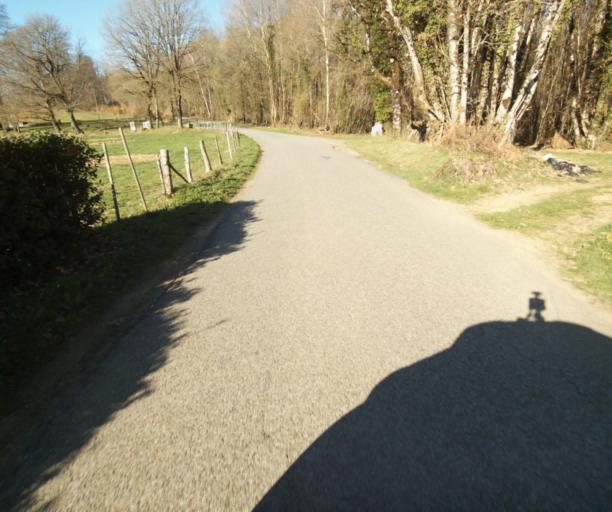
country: FR
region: Limousin
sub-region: Departement de la Correze
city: Saint-Clement
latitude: 45.3877
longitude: 1.6325
